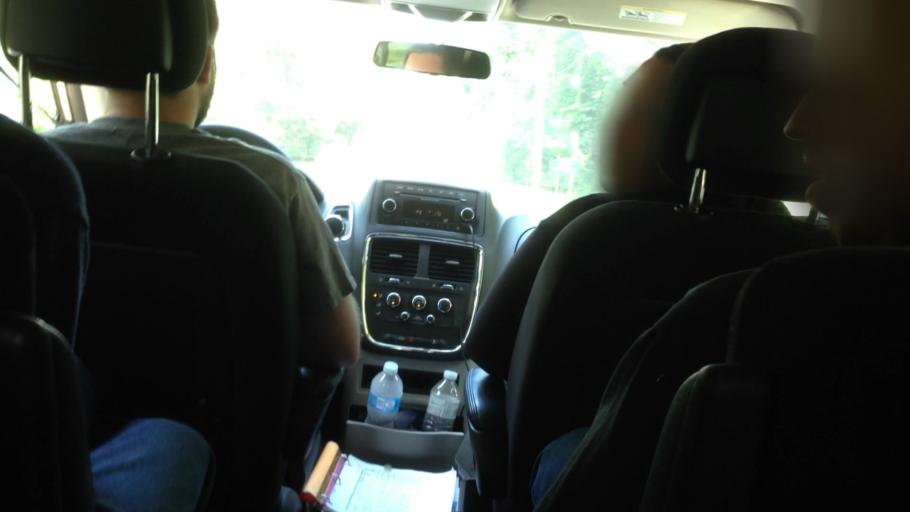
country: US
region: New York
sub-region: Dutchess County
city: Tivoli
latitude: 42.1138
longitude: -73.8919
